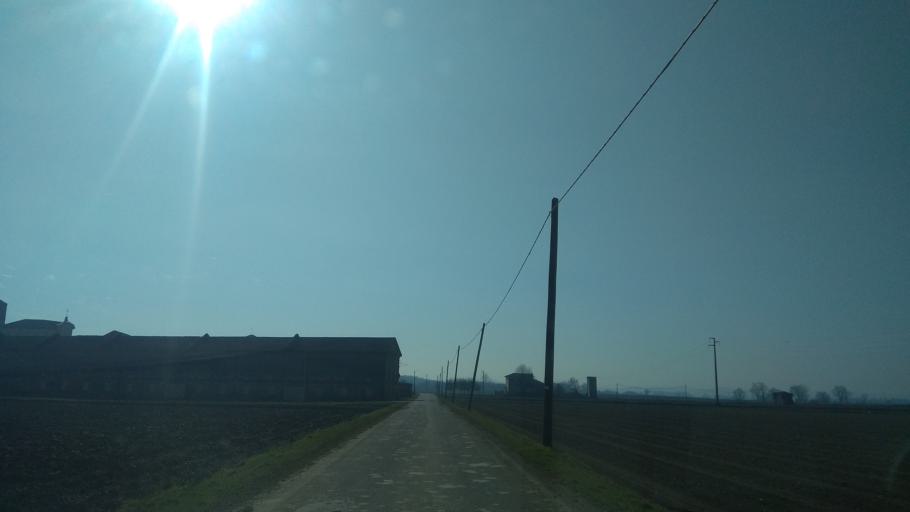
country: IT
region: Piedmont
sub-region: Provincia di Vercelli
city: Ronsecco
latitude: 45.2400
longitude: 8.2333
